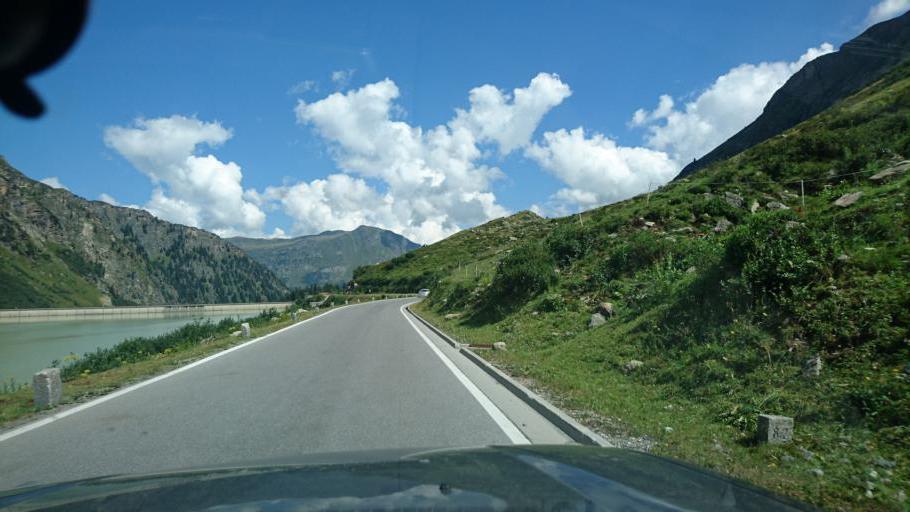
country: AT
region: Vorarlberg
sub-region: Politischer Bezirk Bludenz
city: Gaschurn
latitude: 46.9320
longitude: 10.0581
